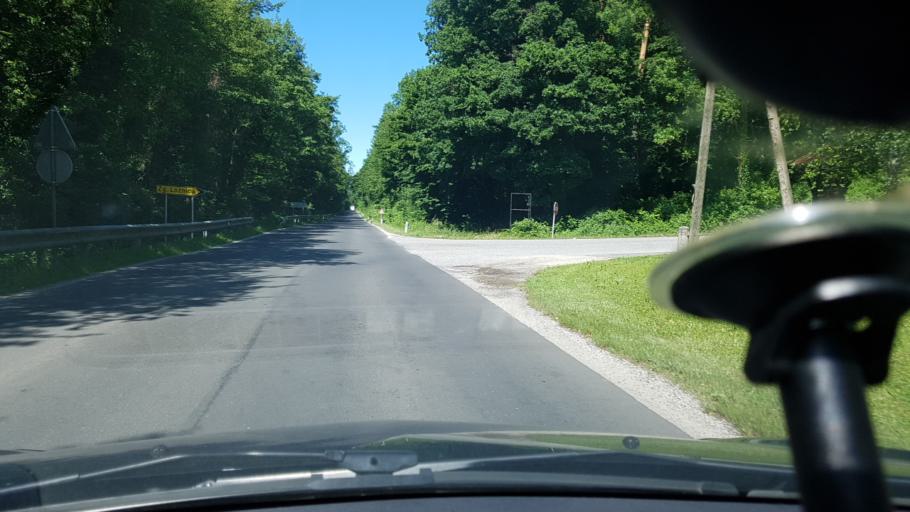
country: SI
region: Slovenska Bistrica
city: Slovenska Bistrica
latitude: 46.3829
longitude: 15.5225
